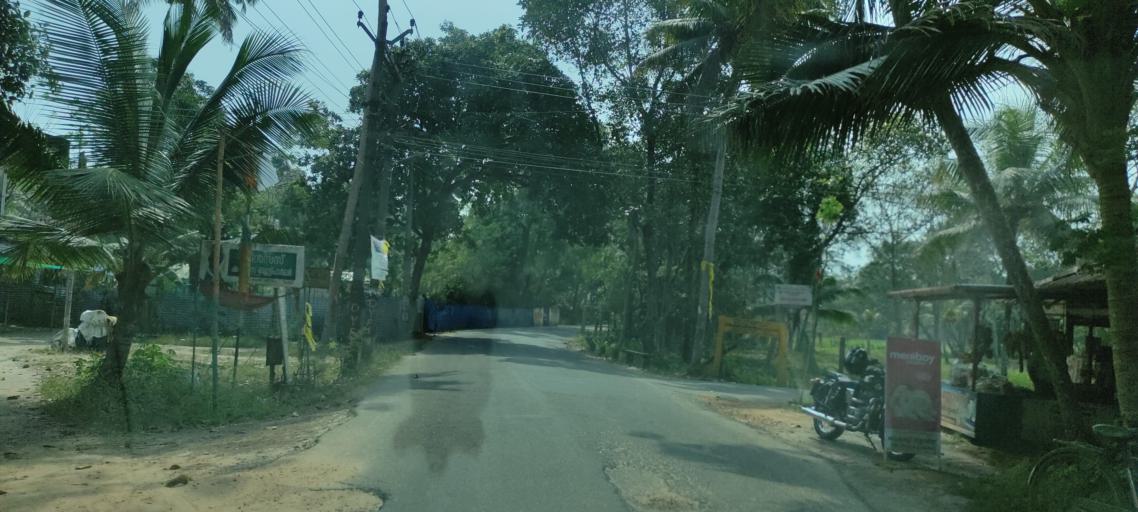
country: IN
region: Kerala
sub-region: Alappuzha
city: Shertallai
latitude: 9.6500
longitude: 76.3566
